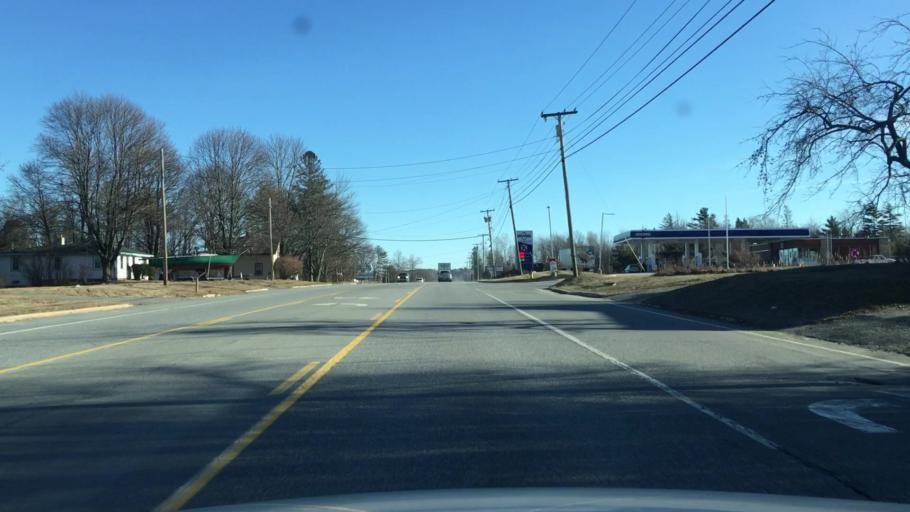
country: US
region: Maine
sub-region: Penobscot County
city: Holden
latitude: 44.7652
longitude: -68.7073
